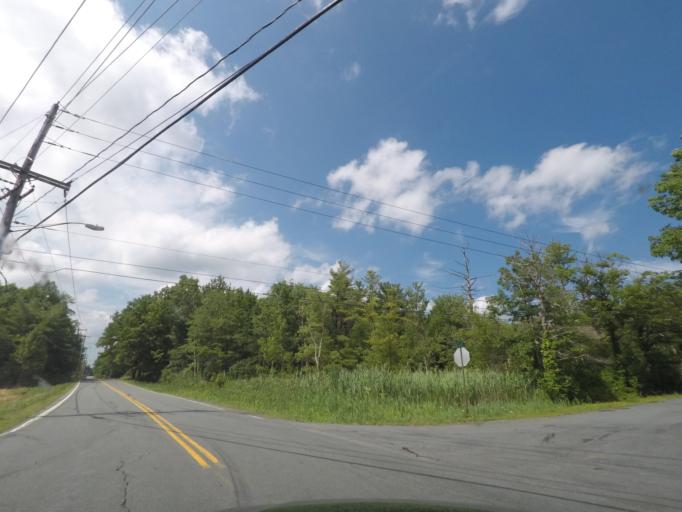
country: US
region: New York
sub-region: Rensselaer County
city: Averill Park
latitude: 42.6240
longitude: -73.5435
